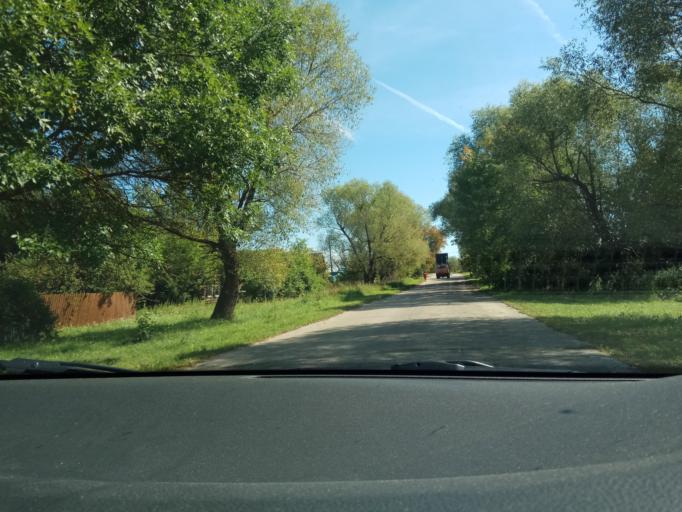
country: RU
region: Vladimir
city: Dobryatino
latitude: 55.7341
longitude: 41.4329
